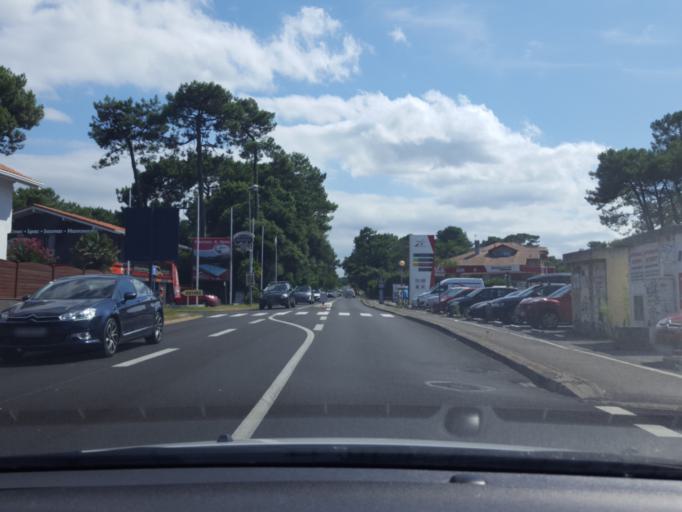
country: FR
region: Aquitaine
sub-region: Departement des Landes
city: Capbreton
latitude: 43.6385
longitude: -1.4260
